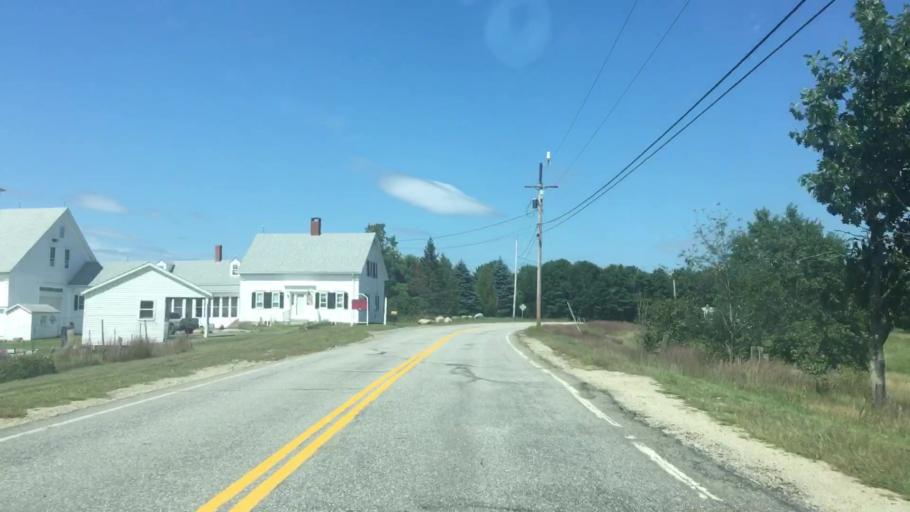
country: US
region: Maine
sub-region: Androscoggin County
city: Lisbon
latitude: 44.0541
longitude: -70.1166
